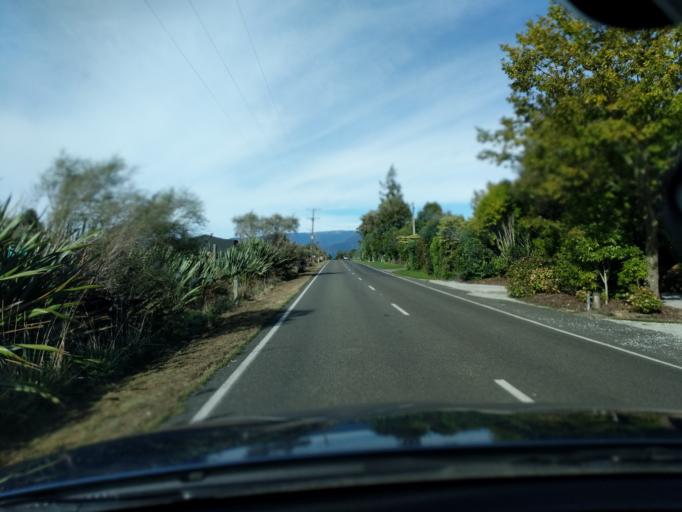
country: NZ
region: Tasman
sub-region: Tasman District
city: Takaka
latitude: -40.8482
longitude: 172.8588
